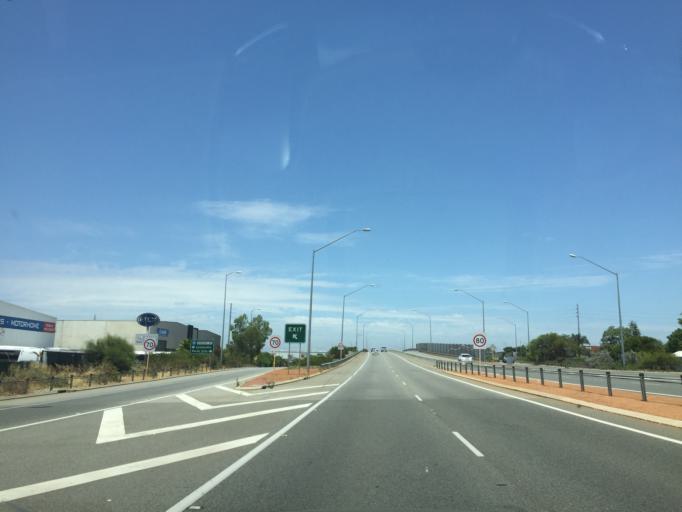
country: AU
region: Western Australia
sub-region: Belmont
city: Kewdale
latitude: -31.9836
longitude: 115.9370
